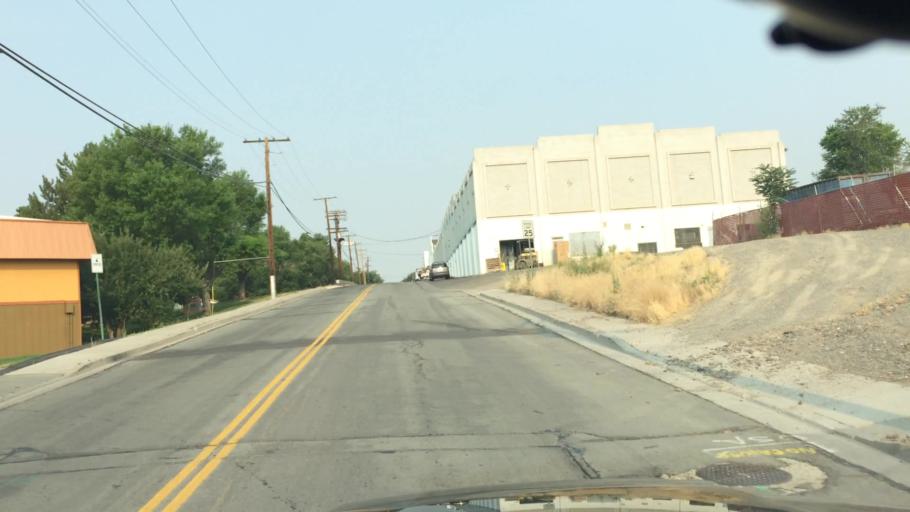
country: US
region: Nevada
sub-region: Washoe County
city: Reno
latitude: 39.5492
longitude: -119.7996
